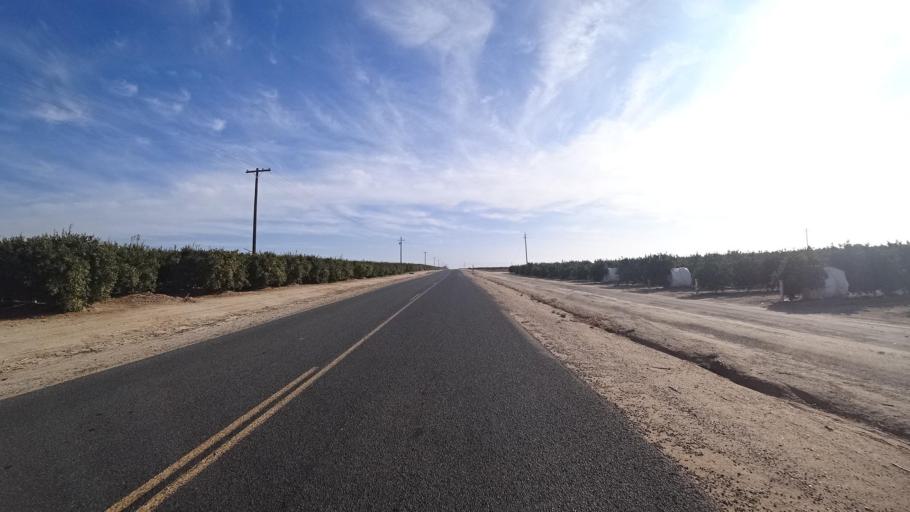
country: US
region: California
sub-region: Kern County
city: McFarland
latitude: 35.6022
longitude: -119.1227
